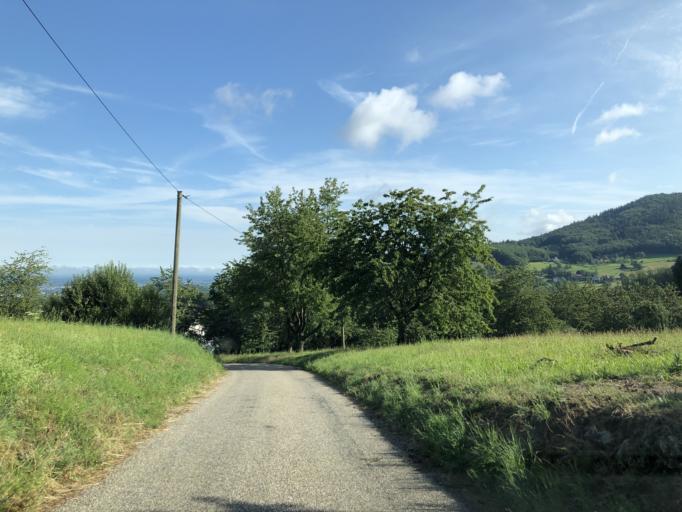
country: DE
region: Baden-Wuerttemberg
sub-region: Freiburg Region
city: Sasbachwalden
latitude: 48.6332
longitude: 8.1455
